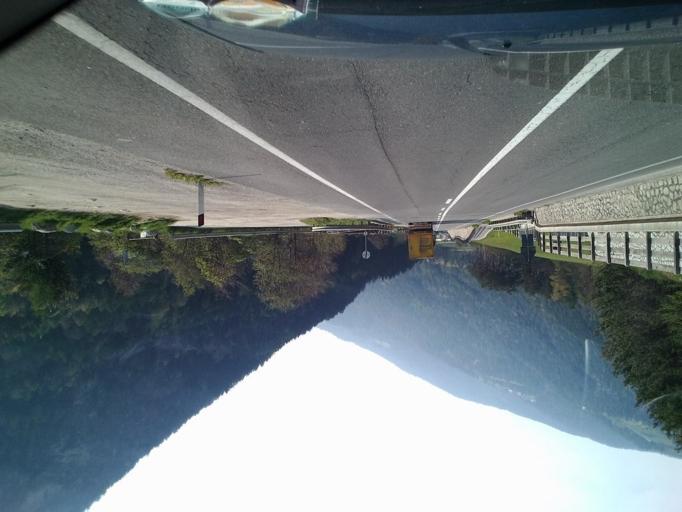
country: IT
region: Trentino-Alto Adige
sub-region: Bolzano
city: Rio di Pusteria
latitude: 46.8063
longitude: 11.6800
